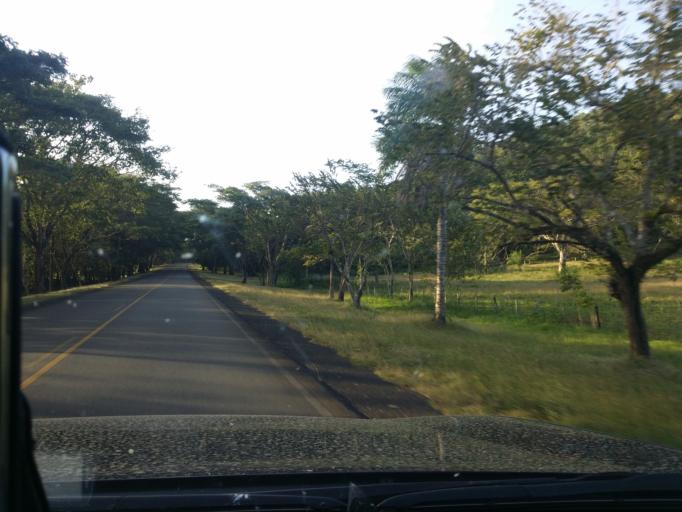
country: NI
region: Rio San Juan
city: San Miguelito
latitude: 11.4003
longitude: -84.8262
